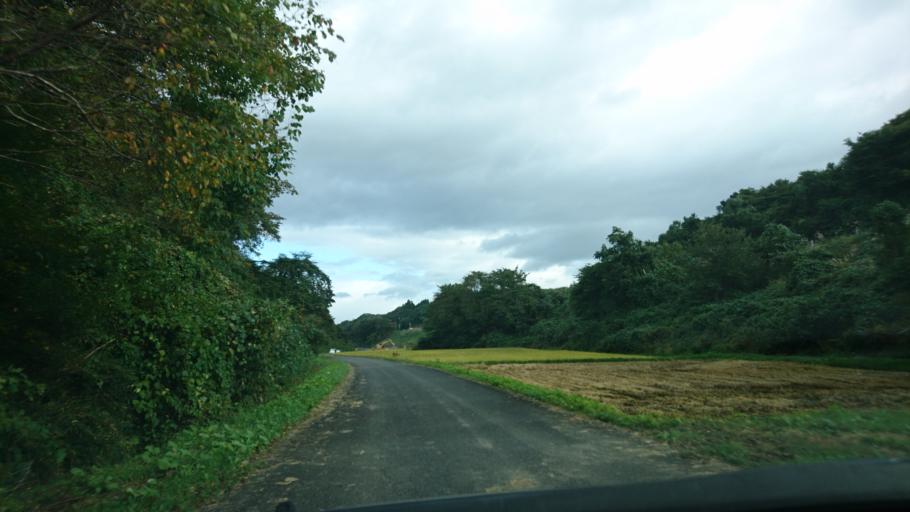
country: JP
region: Iwate
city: Ichinoseki
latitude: 38.8891
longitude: 141.0920
